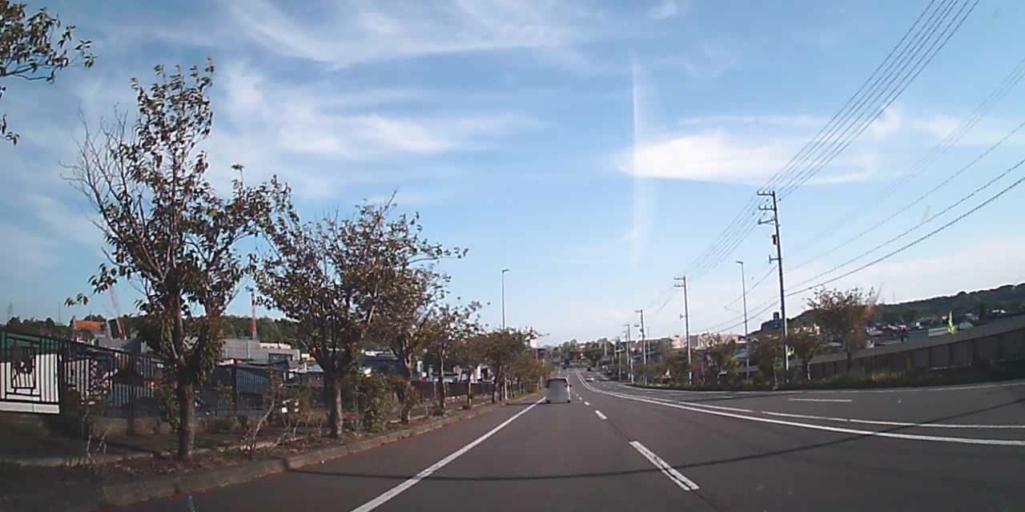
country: JP
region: Hokkaido
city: Shiraoi
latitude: 42.4591
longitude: 141.1776
